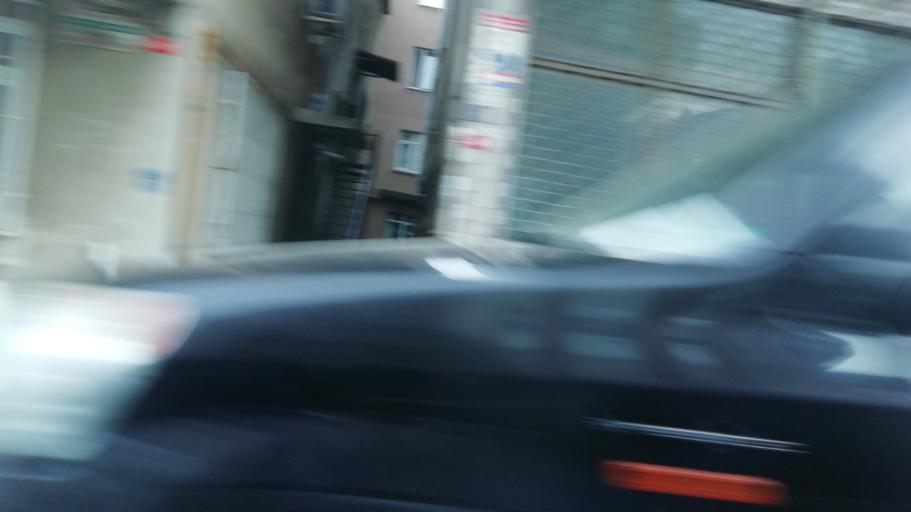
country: TR
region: Istanbul
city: Bagcilar
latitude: 41.0261
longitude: 28.8334
